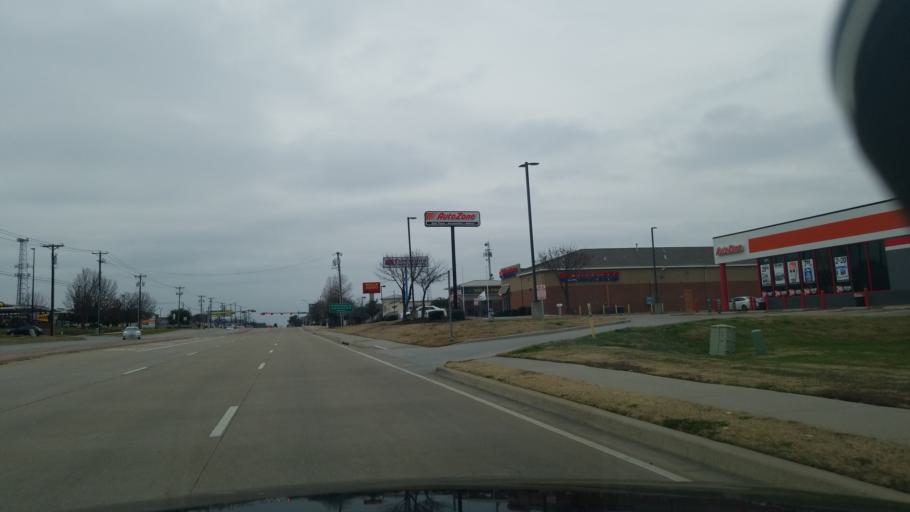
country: US
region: Texas
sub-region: Denton County
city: Hickory Creek
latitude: 33.1301
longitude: -97.0444
